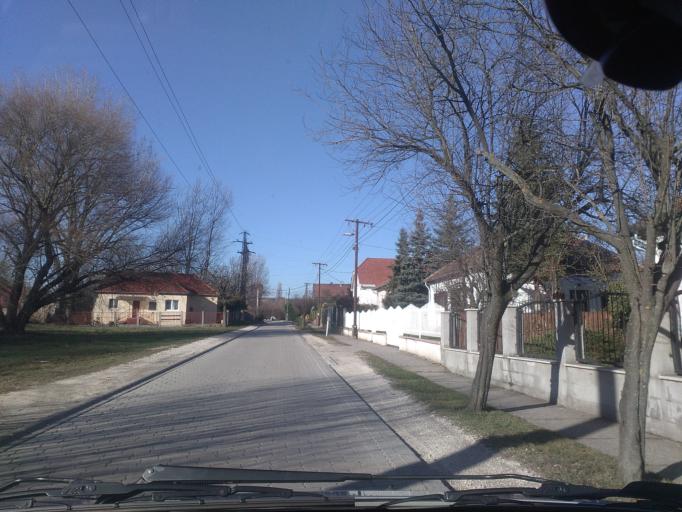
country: HU
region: Pest
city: Pilisvorosvar
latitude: 47.6134
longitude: 18.9115
